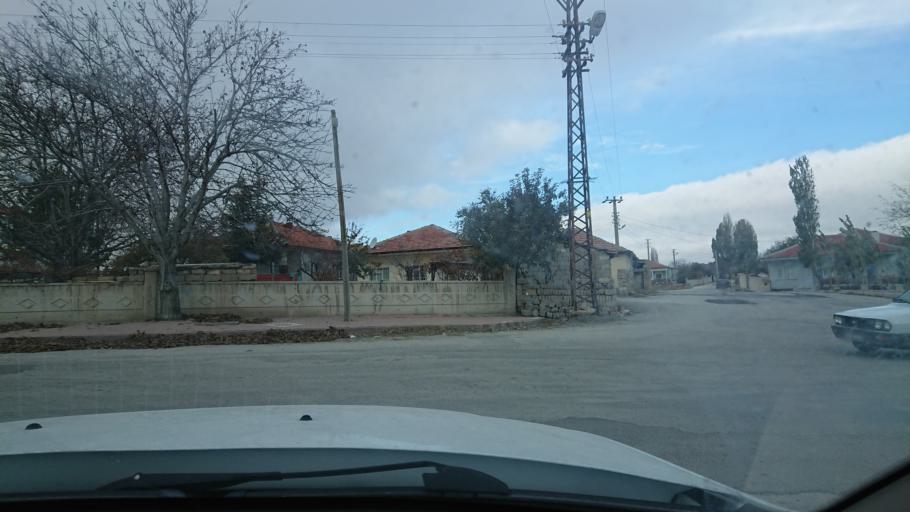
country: TR
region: Aksaray
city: Ortakoy
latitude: 38.7452
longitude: 34.0483
